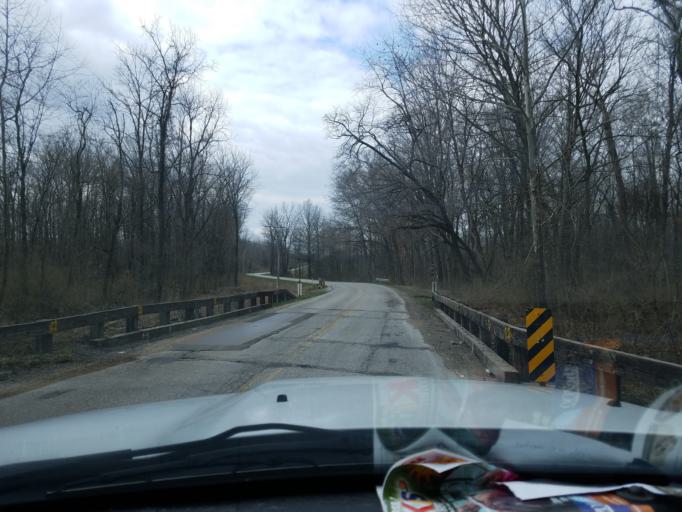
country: US
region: Indiana
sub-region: Vigo County
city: Terre Haute
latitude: 39.4132
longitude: -87.3436
